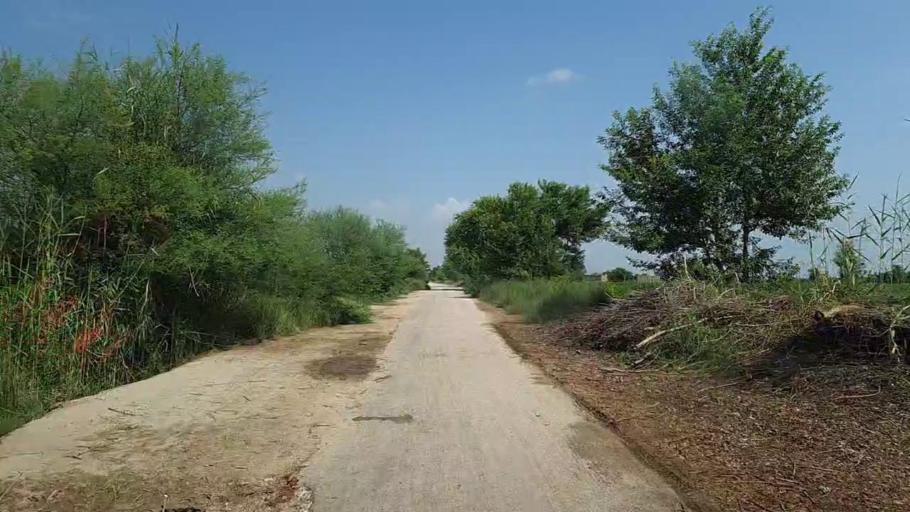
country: PK
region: Sindh
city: Bhiria
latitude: 26.8754
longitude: 68.2487
